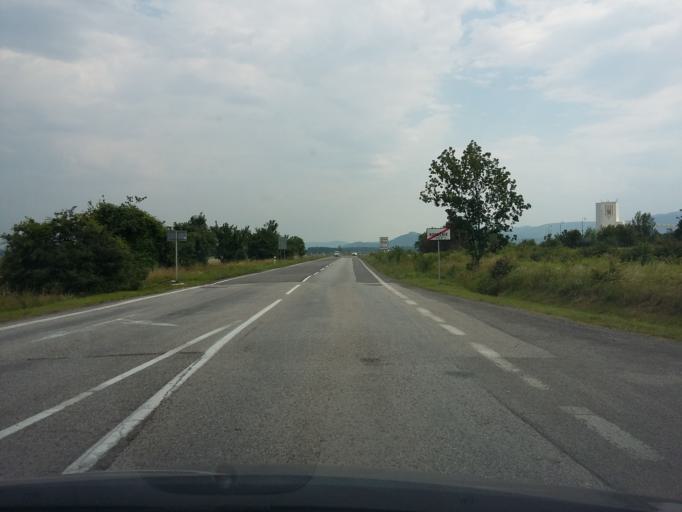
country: SK
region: Bratislavsky
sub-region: Okres Malacky
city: Malacky
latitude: 48.4587
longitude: 17.1784
